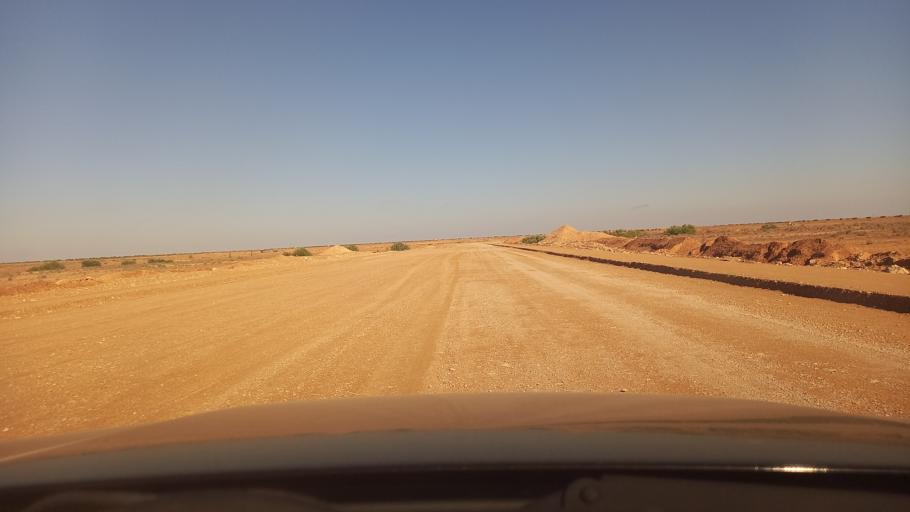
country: TN
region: Madanin
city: Medenine
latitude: 33.1422
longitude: 10.5059
